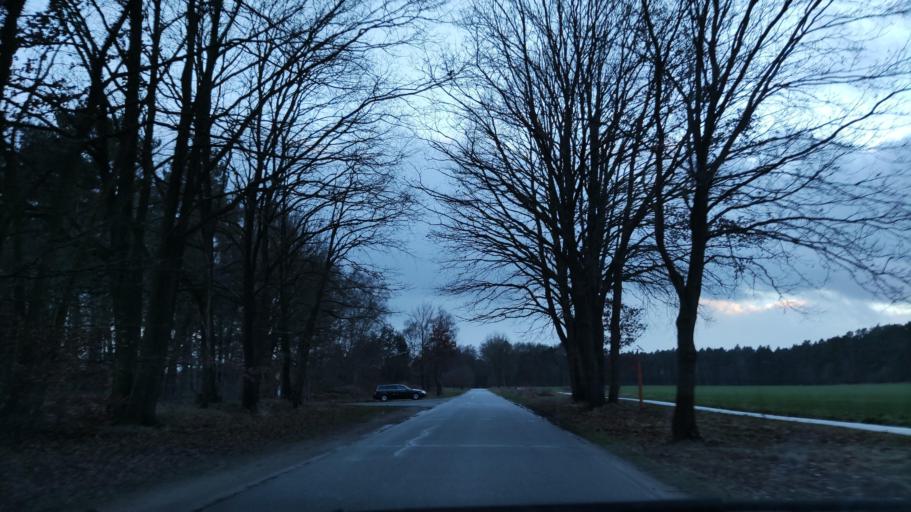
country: DE
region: Lower Saxony
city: Sudergellersen
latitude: 53.2155
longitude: 10.3302
